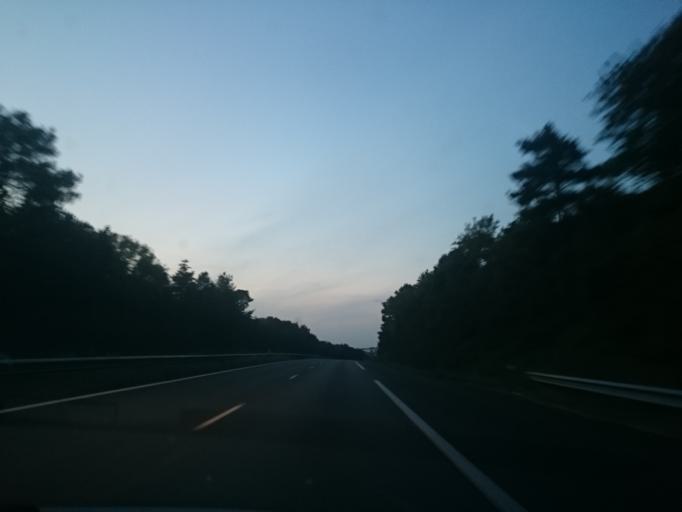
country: FR
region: Brittany
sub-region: Departement du Finistere
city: Hopital-Camfrout
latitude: 48.3283
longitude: -4.2266
